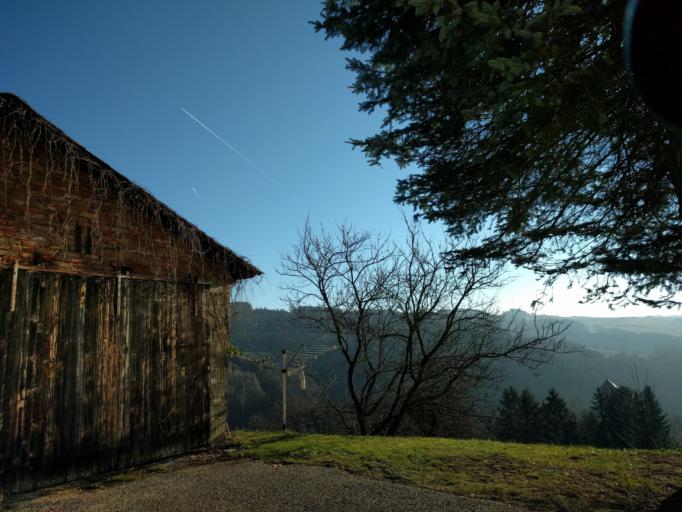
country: AT
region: Upper Austria
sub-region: Politischer Bezirk Urfahr-Umgebung
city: Kirchschlag bei Linz
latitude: 48.4052
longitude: 14.2914
